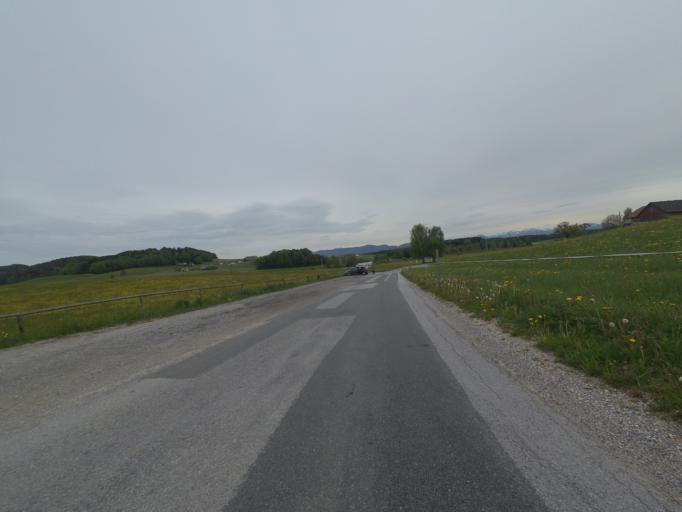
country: AT
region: Salzburg
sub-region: Politischer Bezirk Salzburg-Umgebung
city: Mattsee
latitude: 47.9697
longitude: 13.1216
